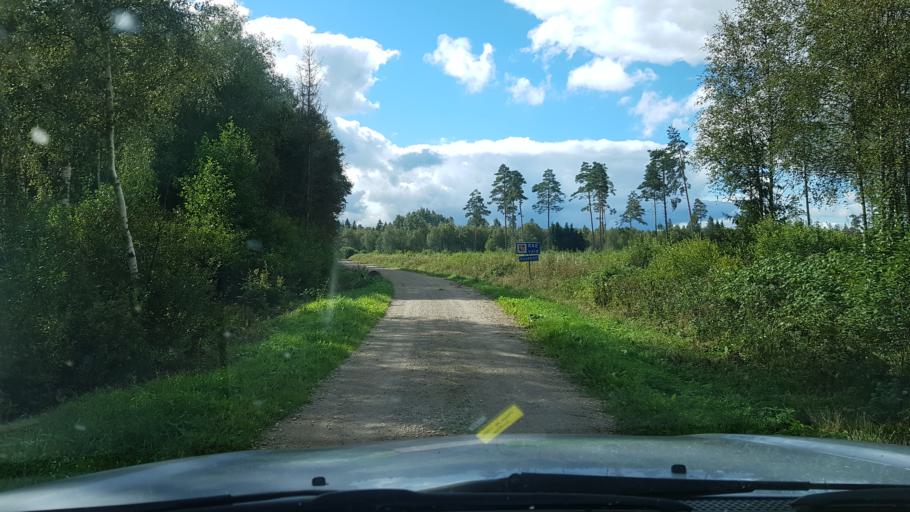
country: EE
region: Harju
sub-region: Raasiku vald
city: Arukula
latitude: 59.3149
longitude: 25.0752
